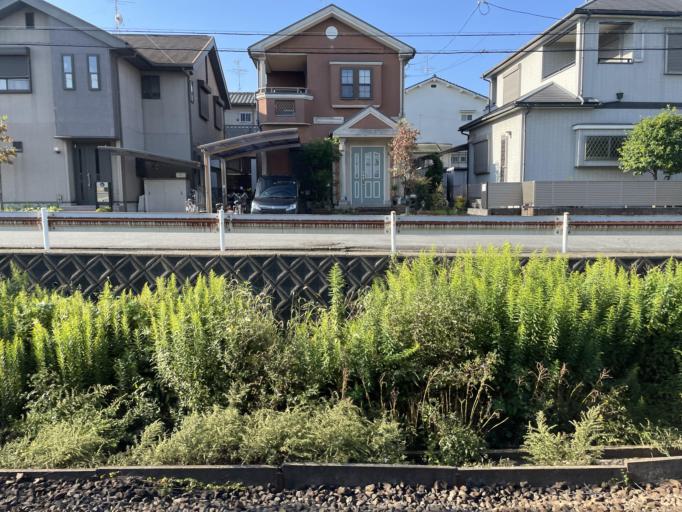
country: JP
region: Osaka
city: Kashihara
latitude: 34.5432
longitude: 135.6983
